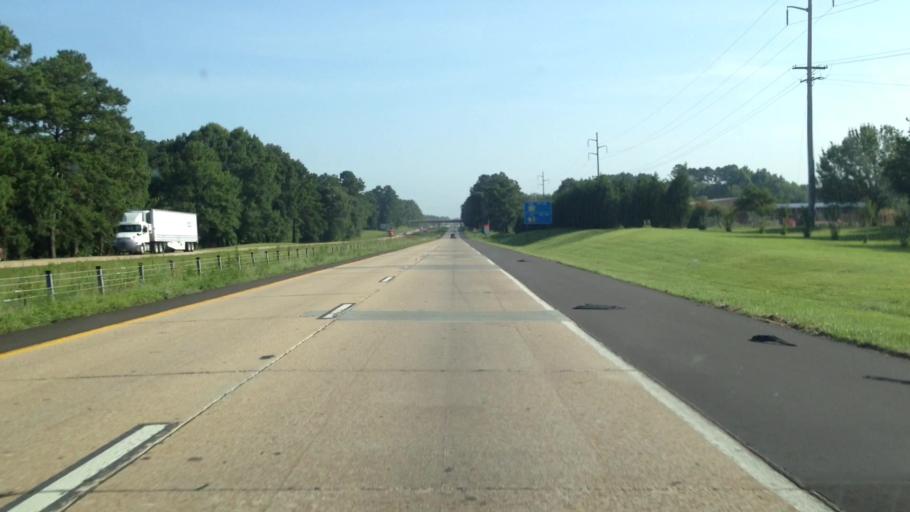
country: US
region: Mississippi
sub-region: Pike County
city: Summit
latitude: 31.2657
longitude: -90.4790
